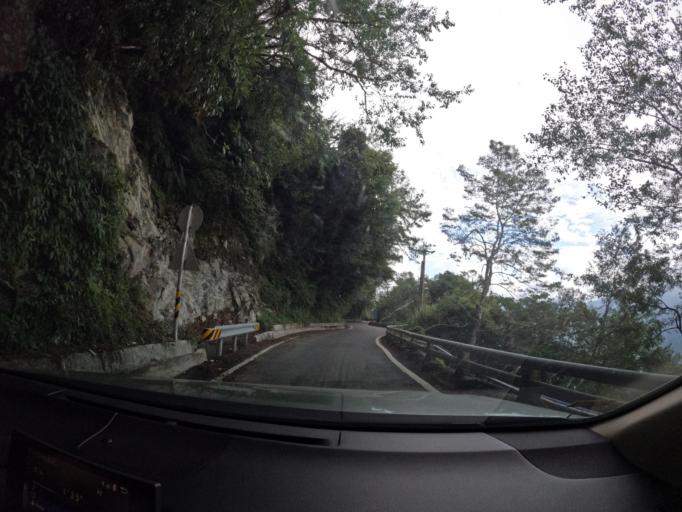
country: TW
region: Taiwan
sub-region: Taitung
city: Taitung
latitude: 23.2419
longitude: 120.9996
